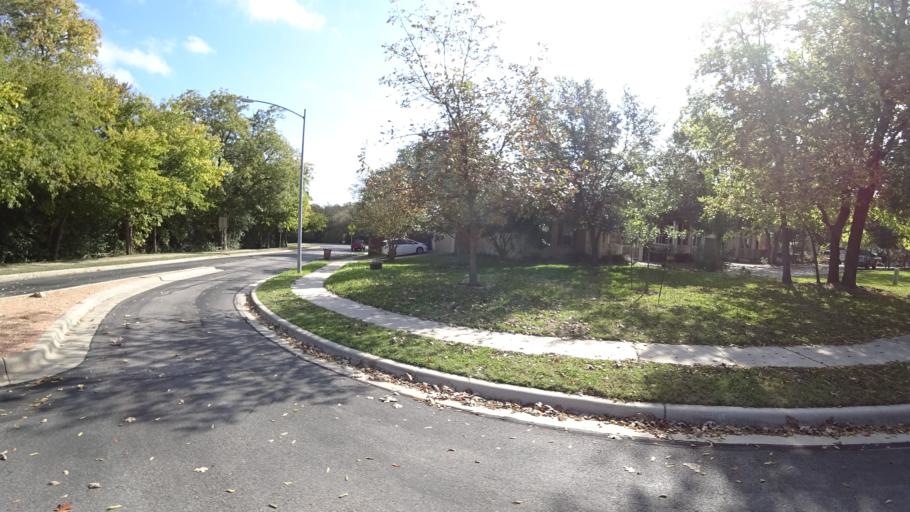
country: US
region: Texas
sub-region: Travis County
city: Shady Hollow
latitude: 30.1915
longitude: -97.8179
